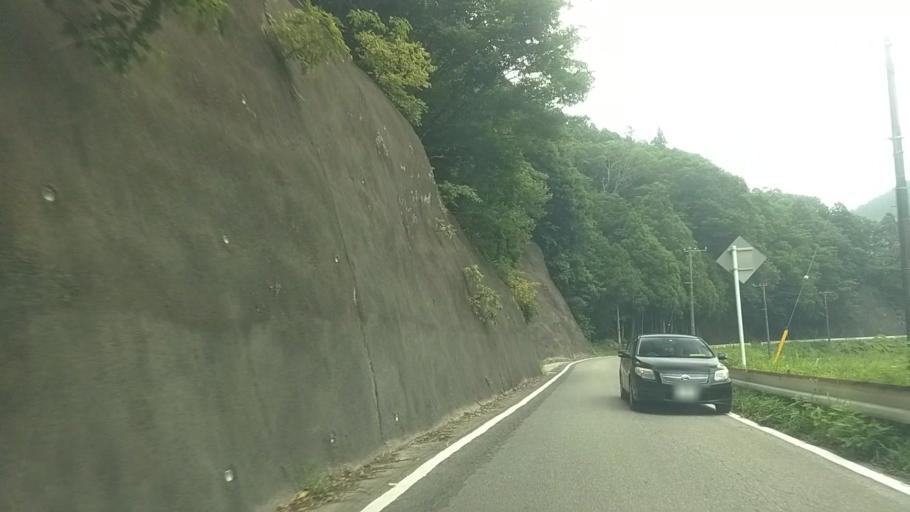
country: JP
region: Chiba
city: Kawaguchi
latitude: 35.2258
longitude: 140.1487
